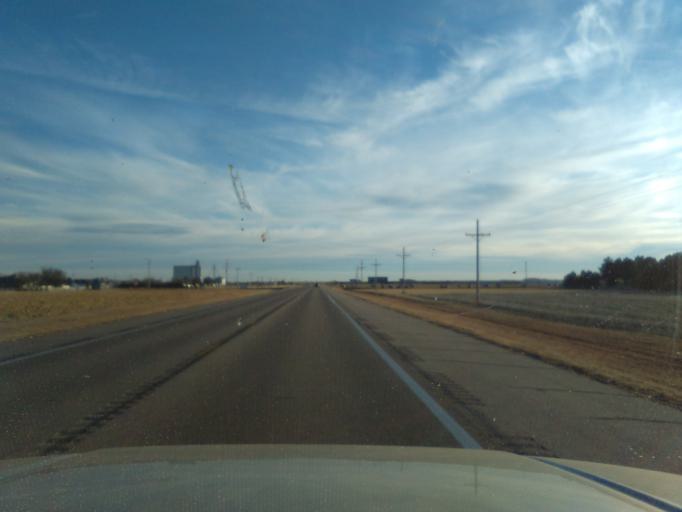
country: US
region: Kansas
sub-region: Logan County
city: Oakley
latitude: 39.1360
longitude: -100.8683
